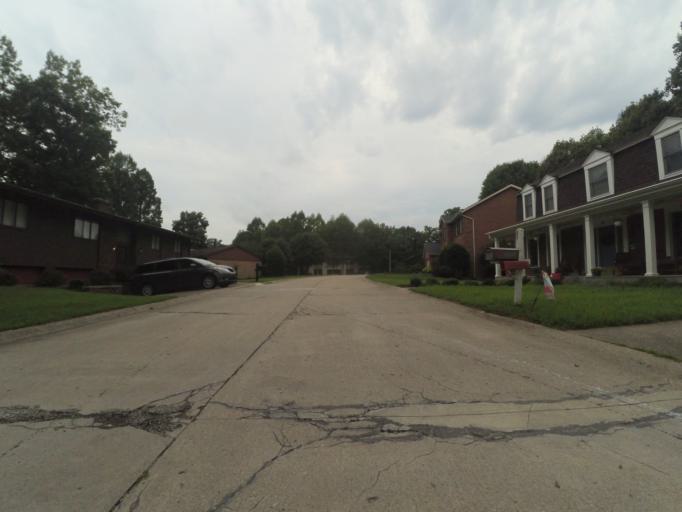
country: US
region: West Virginia
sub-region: Cabell County
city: Huntington
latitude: 38.3997
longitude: -82.3928
